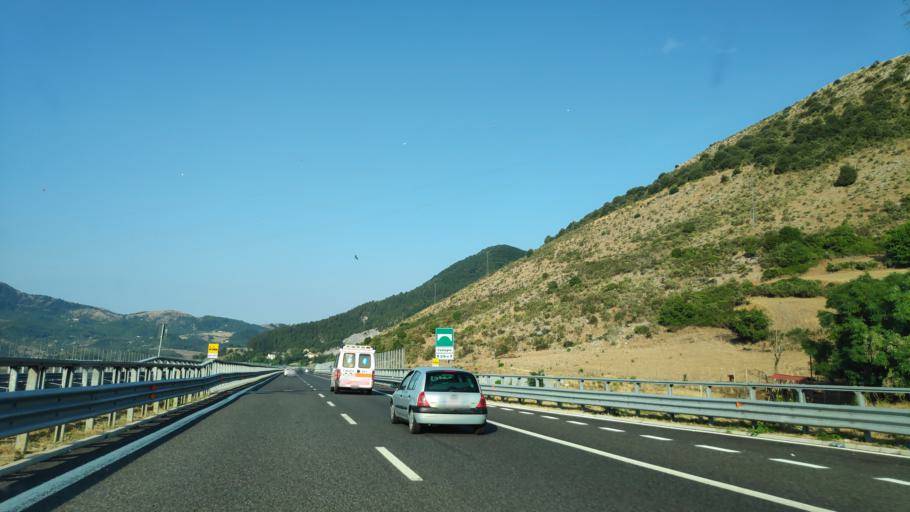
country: IT
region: Calabria
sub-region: Provincia di Cosenza
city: Mormanno
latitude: 39.8859
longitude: 16.0230
